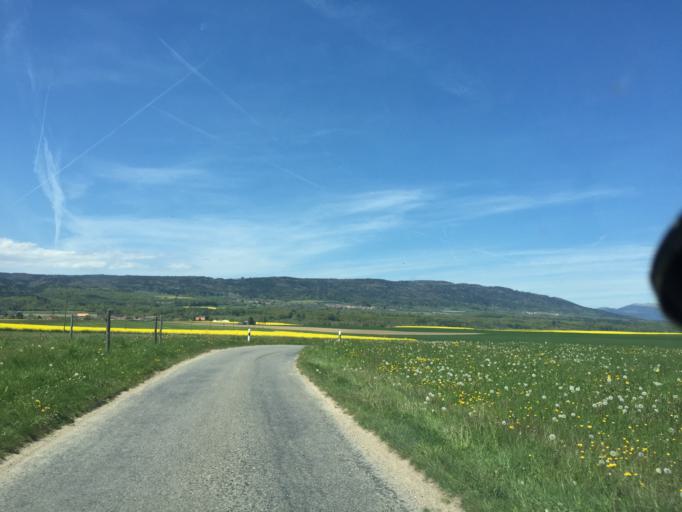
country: CH
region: Vaud
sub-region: Morges District
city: Mauraz
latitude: 46.6067
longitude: 6.4258
